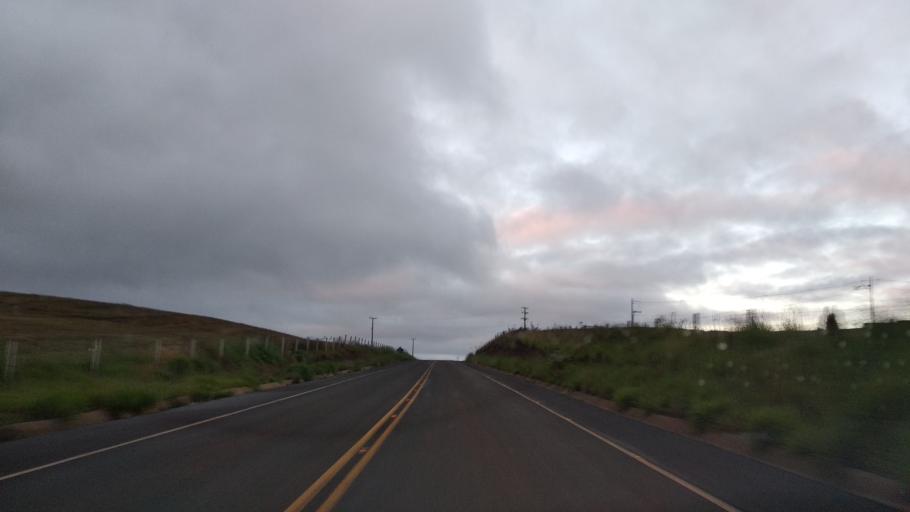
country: BR
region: Santa Catarina
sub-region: Campos Novos
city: Campos Novos
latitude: -27.3688
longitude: -51.2040
